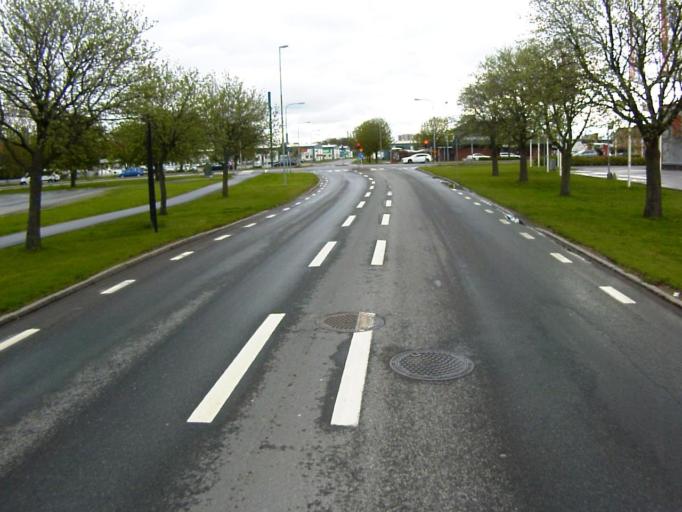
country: SE
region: Skane
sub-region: Kristianstads Kommun
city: Kristianstad
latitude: 56.0233
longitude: 14.1414
